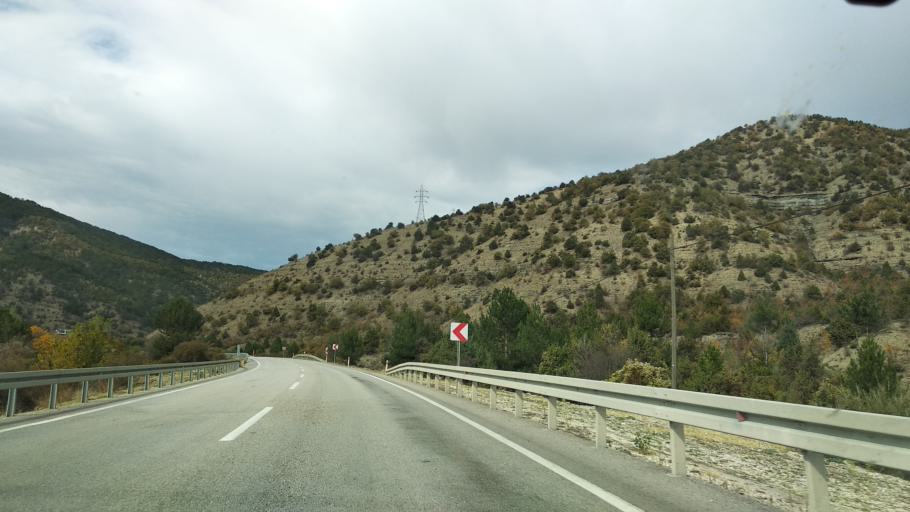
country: TR
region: Bolu
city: Mudurnu
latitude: 40.3375
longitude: 31.2484
